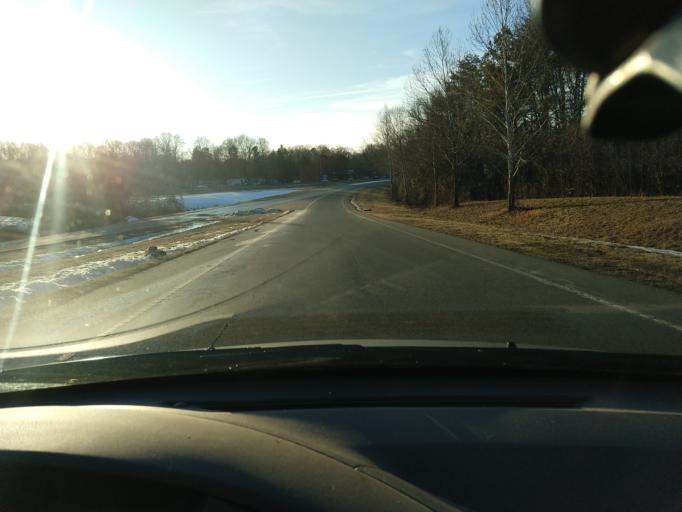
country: US
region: North Carolina
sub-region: Guilford County
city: Greensboro
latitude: 36.0377
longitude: -79.8202
